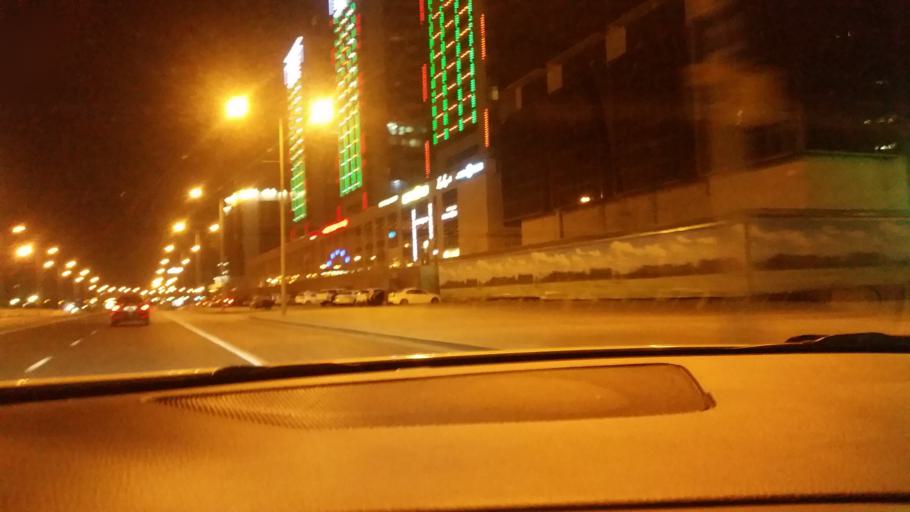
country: KZ
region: Astana Qalasy
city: Astana
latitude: 51.1300
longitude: 71.4585
